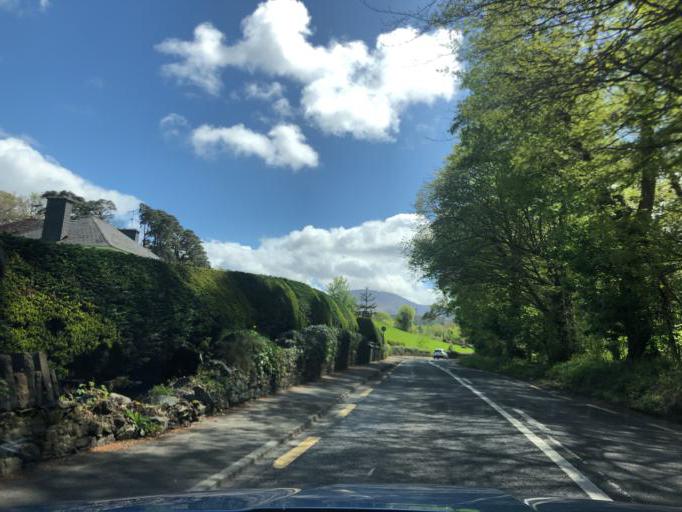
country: IE
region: Munster
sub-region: Ciarrai
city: Cill Airne
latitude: 52.0300
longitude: -9.4891
